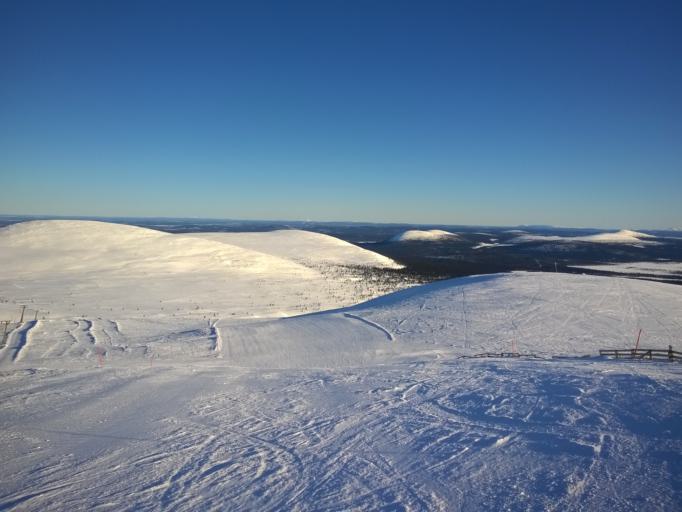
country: FI
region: Lapland
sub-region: Tunturi-Lappi
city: Muonio
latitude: 68.0616
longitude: 24.0334
